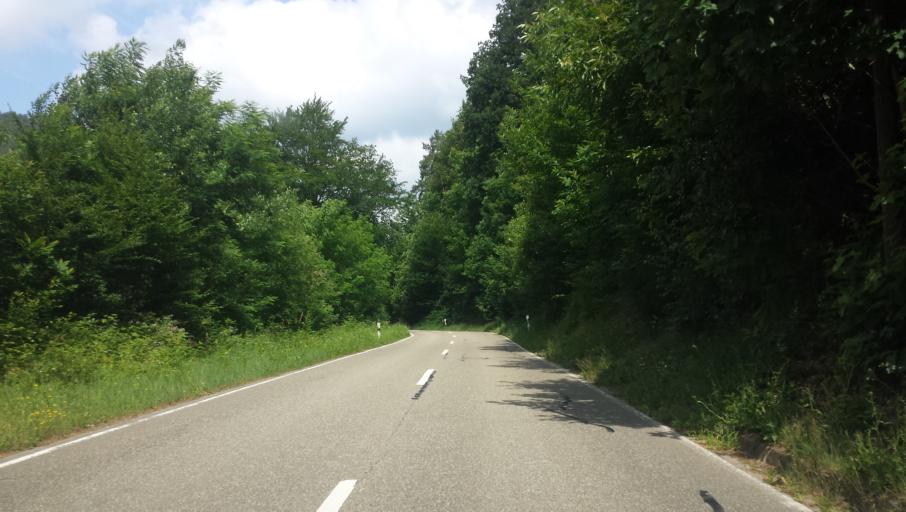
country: DE
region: Rheinland-Pfalz
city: Gleisweiler
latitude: 49.2636
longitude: 8.0611
